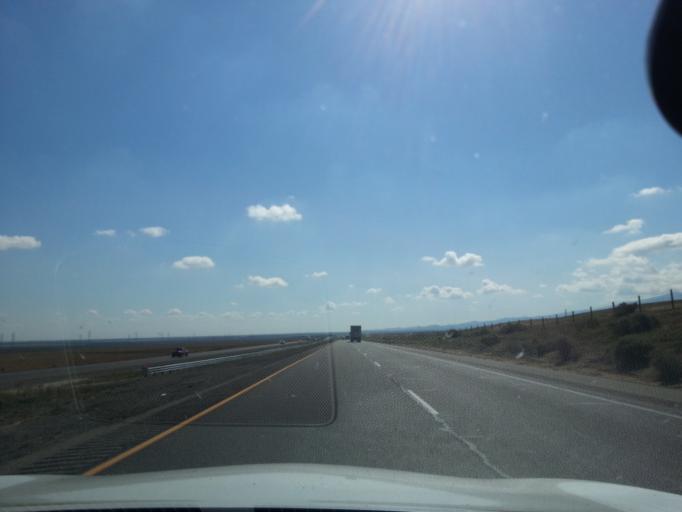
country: US
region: California
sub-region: Fresno County
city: San Joaquin
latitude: 36.4741
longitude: -120.4301
